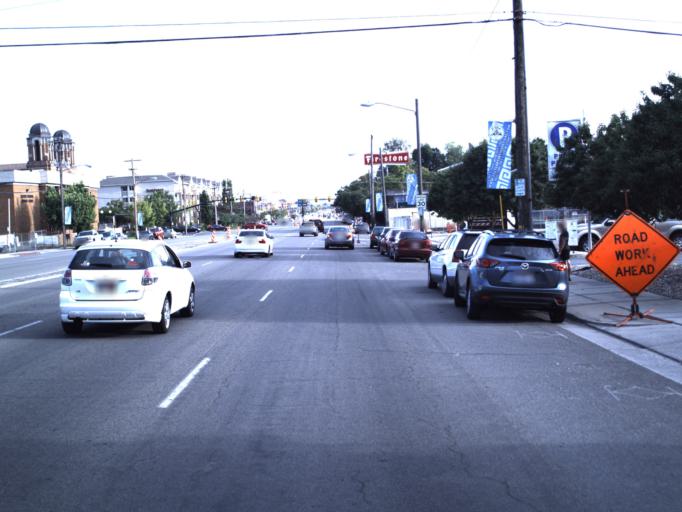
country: US
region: Utah
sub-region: Salt Lake County
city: Salt Lake City
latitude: 40.7646
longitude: -111.8998
